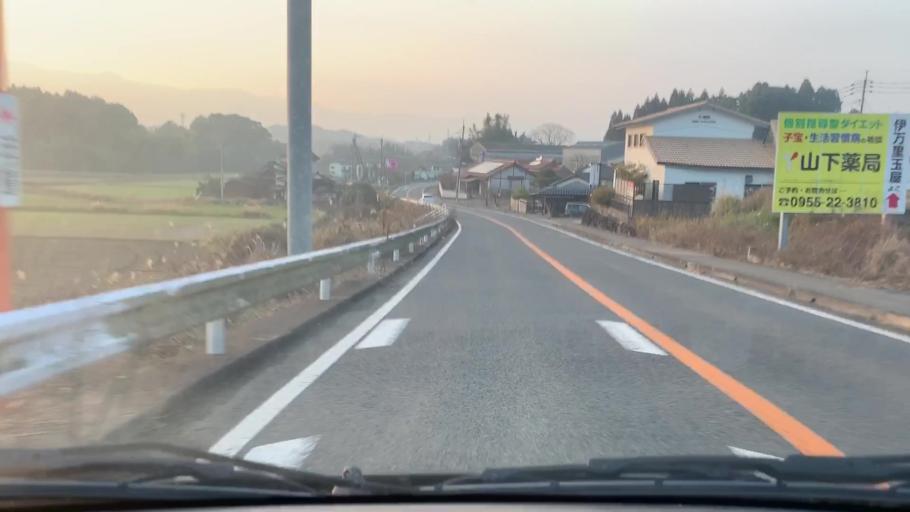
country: JP
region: Saga Prefecture
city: Imaricho-ko
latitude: 33.2650
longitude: 129.9060
